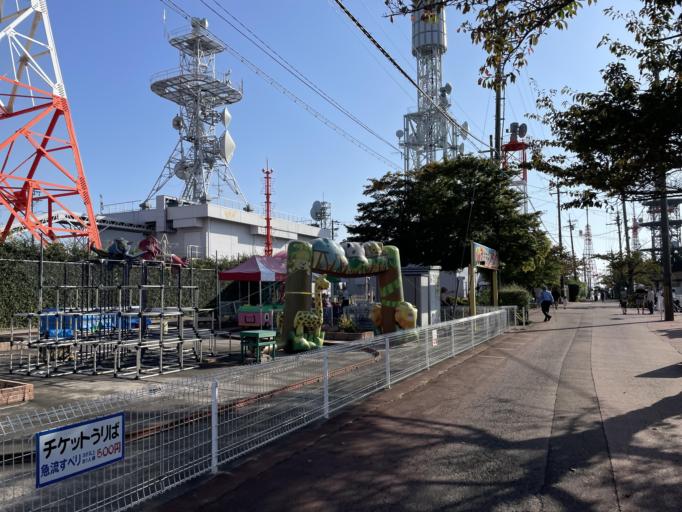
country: JP
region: Nara
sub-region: Ikoma-shi
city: Ikoma
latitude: 34.6778
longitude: 135.6790
